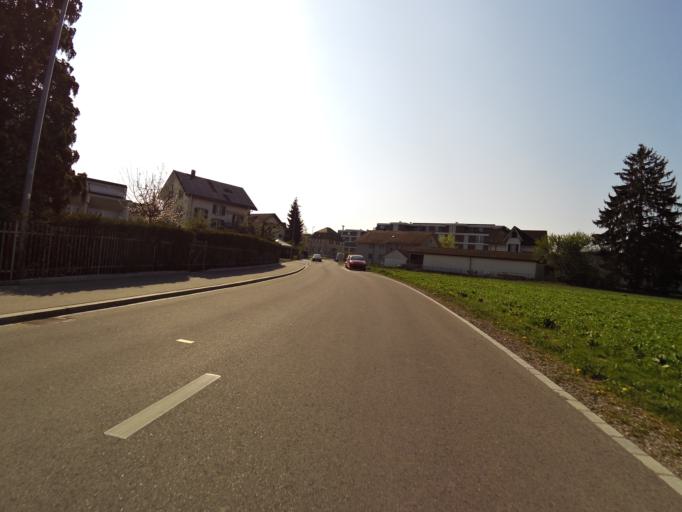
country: CH
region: Thurgau
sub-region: Frauenfeld District
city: Frauenfeld
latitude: 47.5575
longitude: 8.8876
